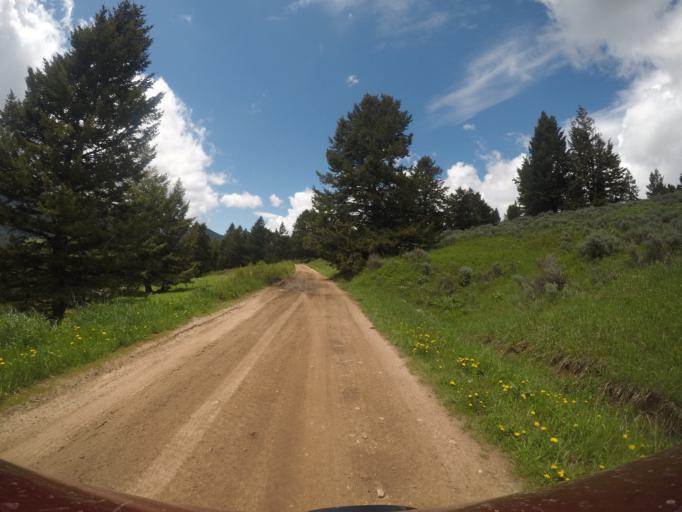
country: US
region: Wyoming
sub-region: Big Horn County
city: Lovell
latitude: 45.1710
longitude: -108.4299
